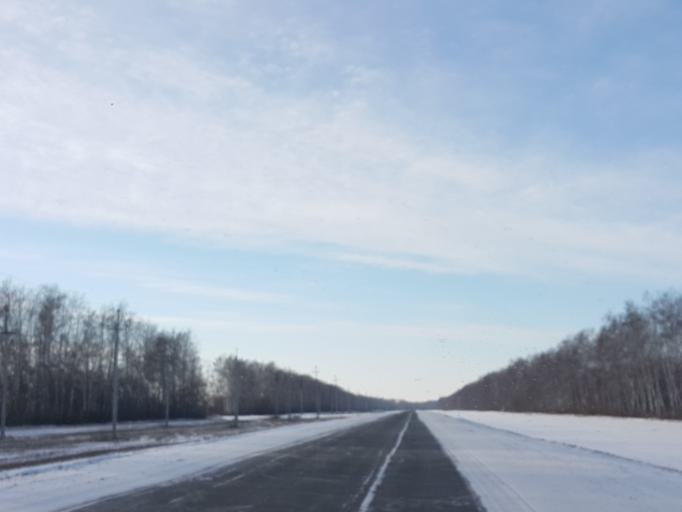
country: RU
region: Tambov
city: Znamenka
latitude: 52.3898
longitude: 41.3489
